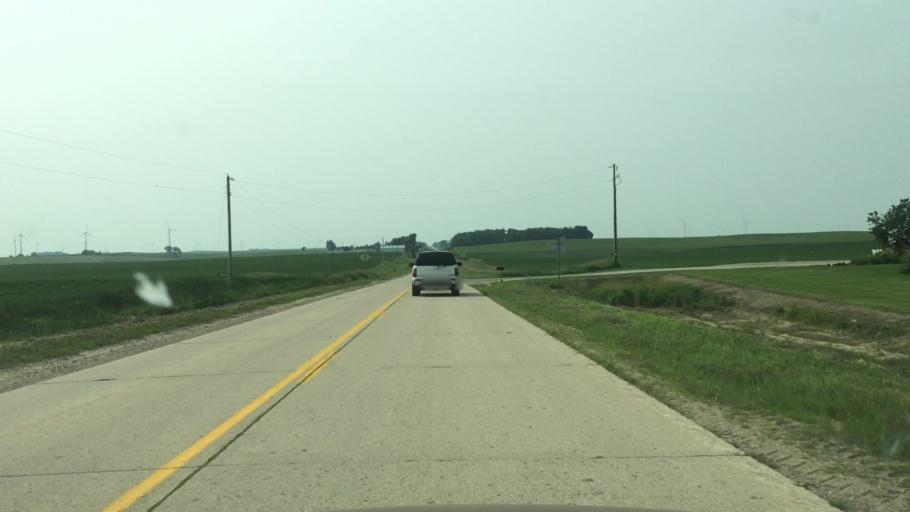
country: US
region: Iowa
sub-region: Dickinson County
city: Lake Park
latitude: 43.4289
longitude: -95.2891
